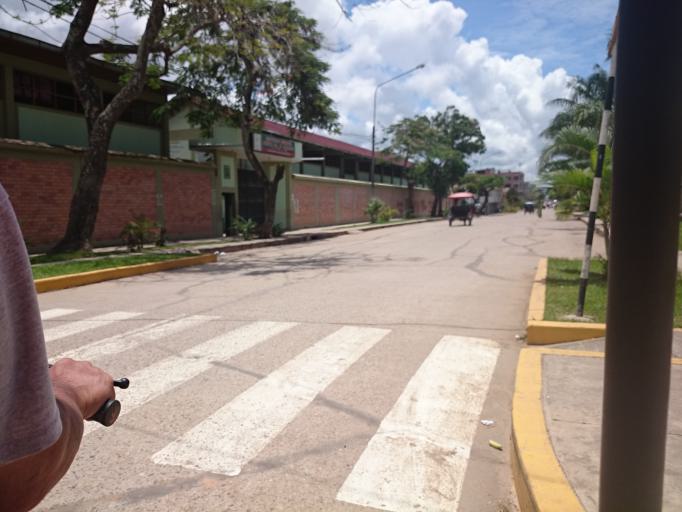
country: PE
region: Ucayali
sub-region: Provincia de Coronel Portillo
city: Pucallpa
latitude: -8.3816
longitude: -74.5279
